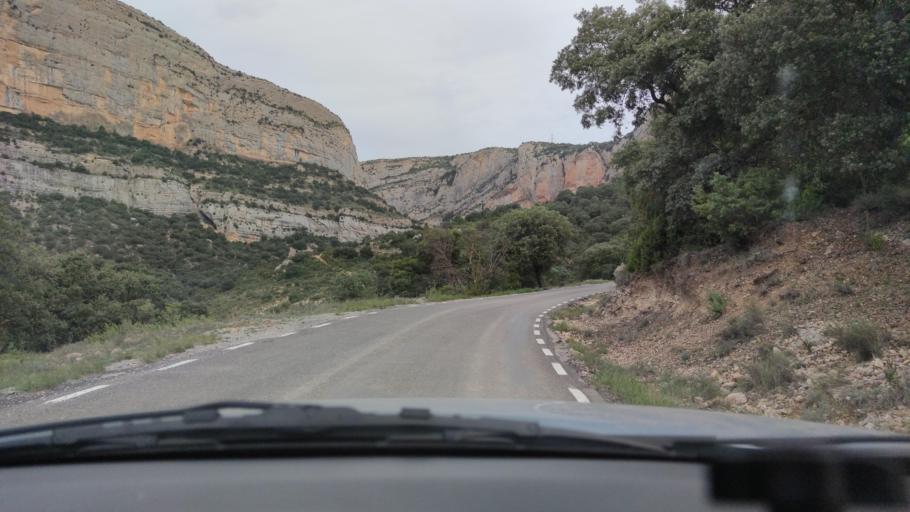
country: ES
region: Catalonia
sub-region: Provincia de Lleida
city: Artesa de Segre
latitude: 42.0167
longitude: 1.0337
